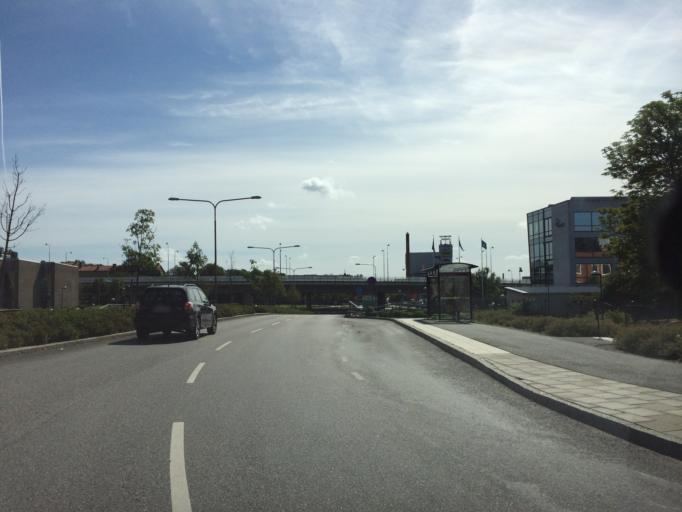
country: SE
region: Stockholm
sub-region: Stockholms Kommun
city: Arsta
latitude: 59.2964
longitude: 18.0004
